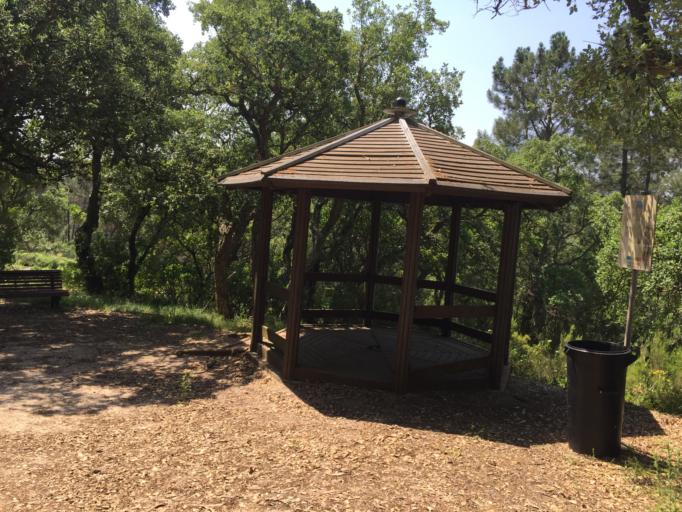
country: PT
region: Lisbon
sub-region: Mafra
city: Milharado
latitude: 38.9039
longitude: -9.1835
